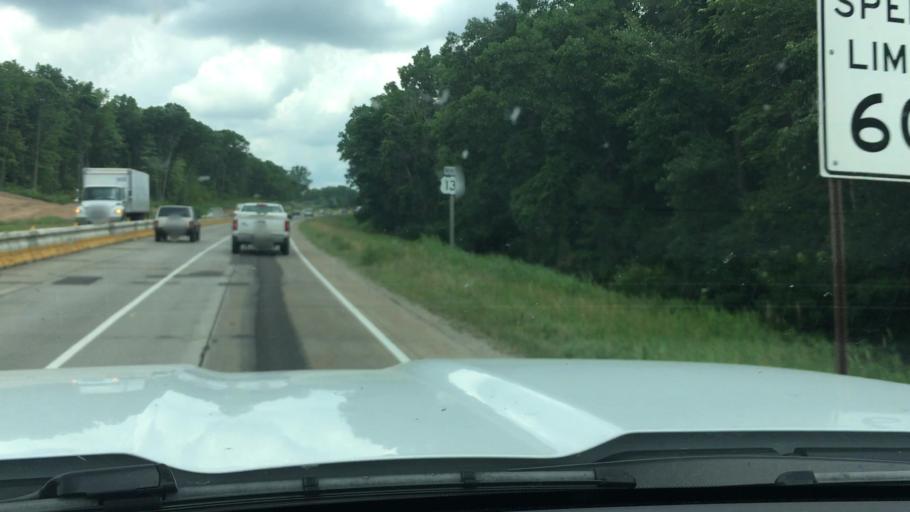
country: US
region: Michigan
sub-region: Kent County
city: Rockford
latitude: 43.1252
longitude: -85.6021
